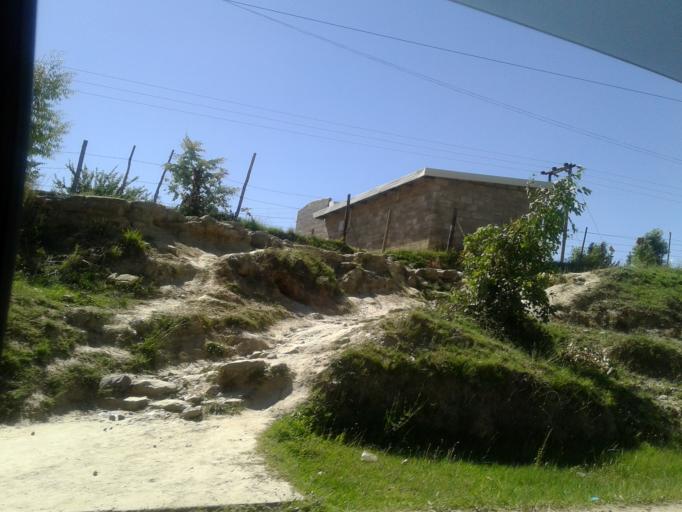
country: LS
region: Butha-Buthe
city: Butha-Buthe
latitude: -28.7626
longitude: 28.2554
